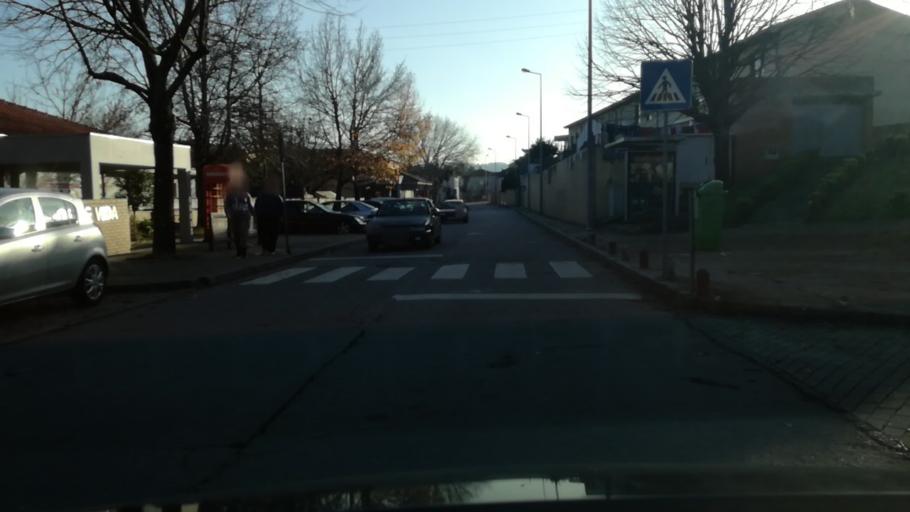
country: PT
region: Braga
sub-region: Vila Nova de Famalicao
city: Ferreiros
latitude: 41.3517
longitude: -8.5295
